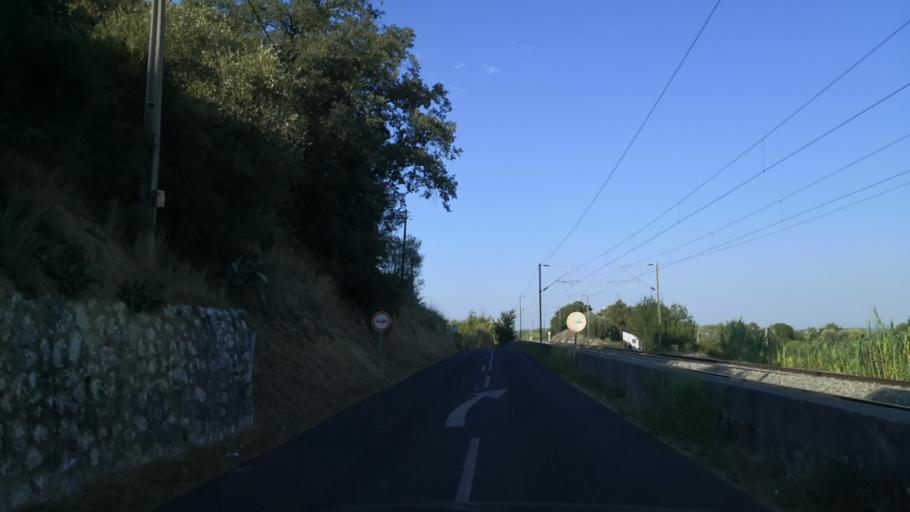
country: PT
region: Santarem
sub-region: Santarem
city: Santarem
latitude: 39.2624
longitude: -8.6659
